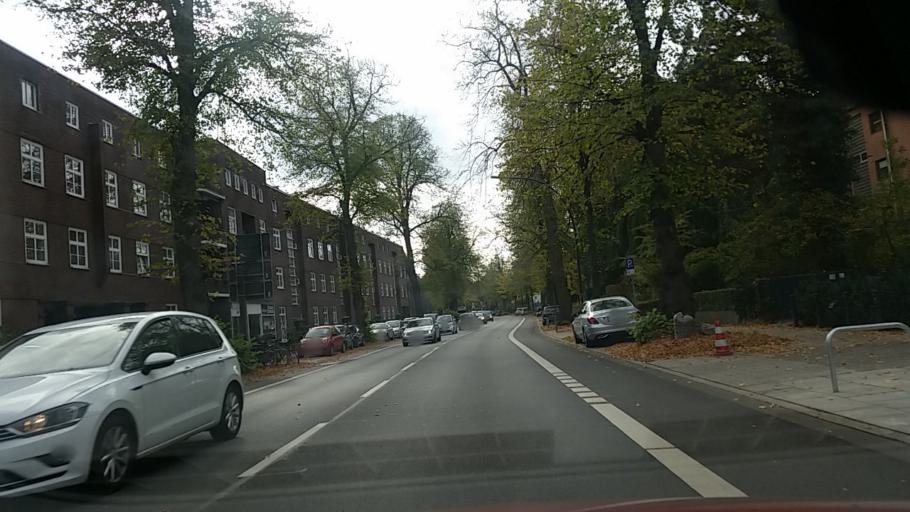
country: DE
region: Hamburg
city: Ohlsdorf
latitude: 53.6251
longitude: 10.0264
